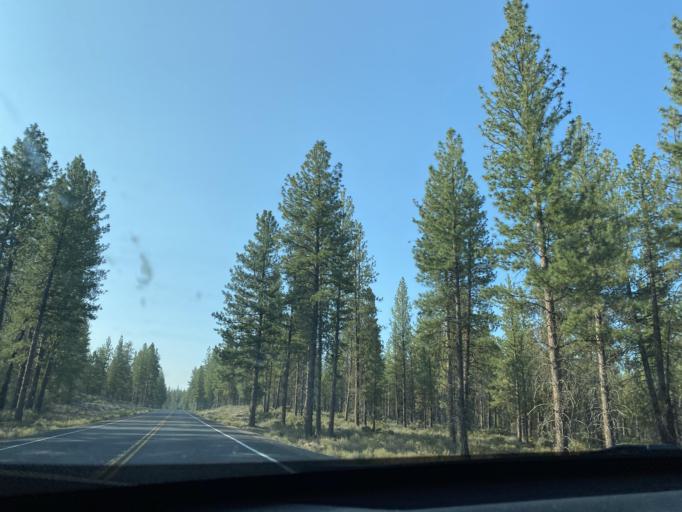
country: US
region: Oregon
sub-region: Deschutes County
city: La Pine
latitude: 43.7178
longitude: -121.4138
